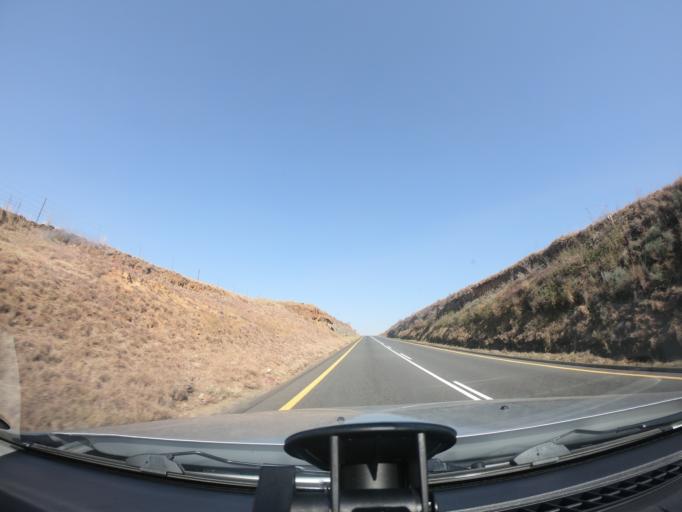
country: ZA
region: KwaZulu-Natal
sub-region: uThukela District Municipality
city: Ekuvukeni
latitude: -28.3512
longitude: 29.9643
